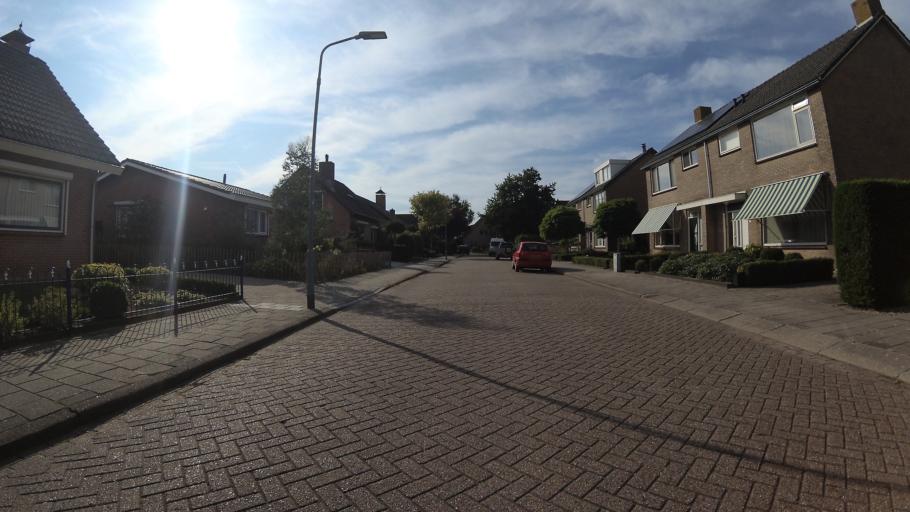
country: NL
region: Zeeland
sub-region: Gemeente Veere
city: Veere
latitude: 51.5756
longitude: 3.6118
